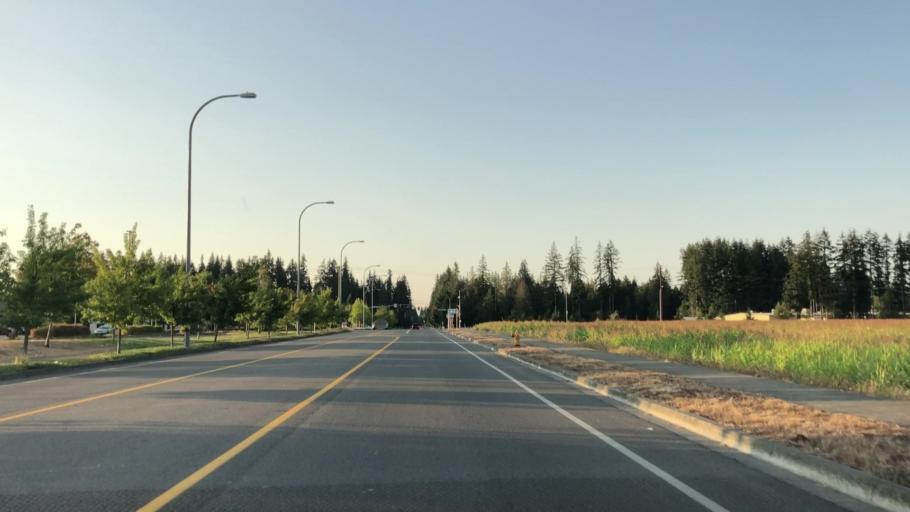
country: US
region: Washington
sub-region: Snohomish County
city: Smokey Point
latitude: 48.1501
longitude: -122.1723
